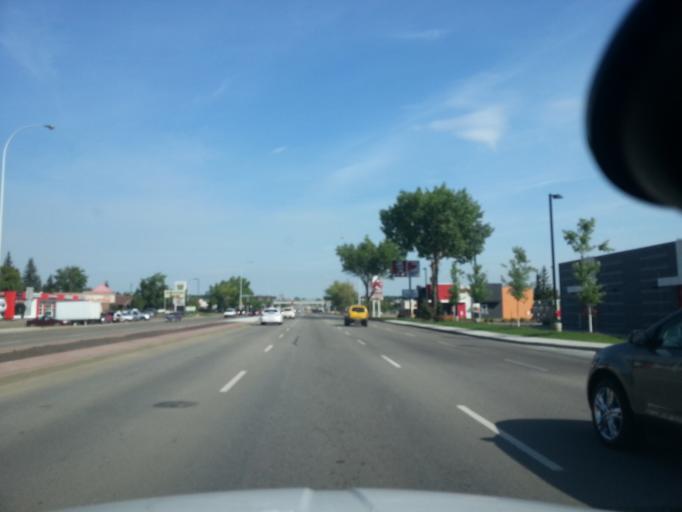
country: CA
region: Alberta
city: St. Albert
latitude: 53.6384
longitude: -113.6243
